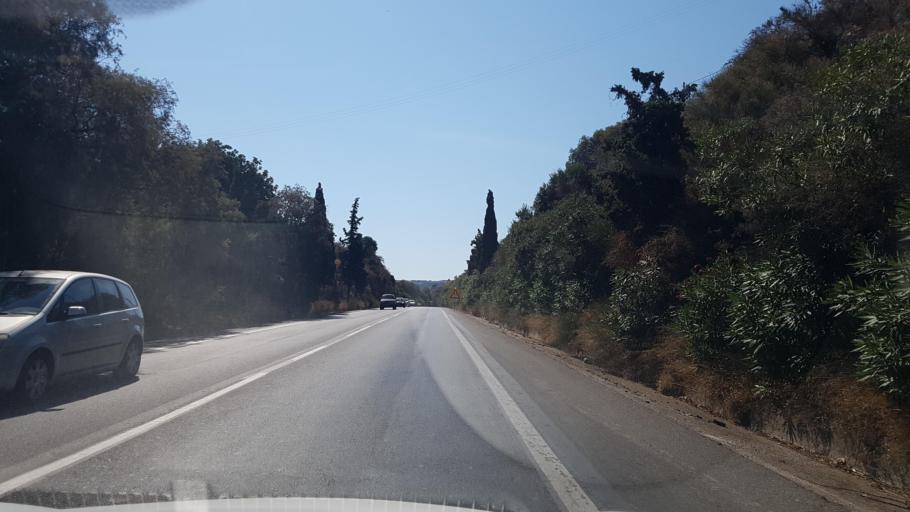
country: GR
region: Crete
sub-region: Nomos Chanias
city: Souda
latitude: 35.4770
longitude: 24.1042
